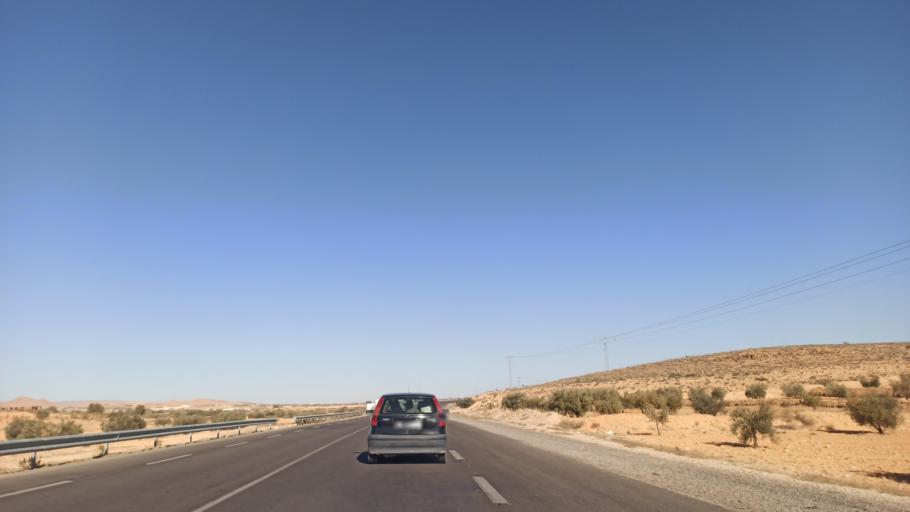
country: TN
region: Sidi Bu Zayd
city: Bi'r al Hufayy
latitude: 34.7216
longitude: 9.0608
